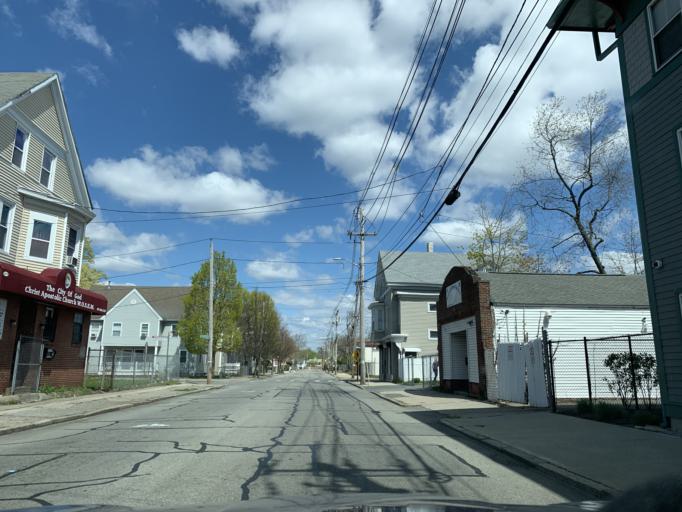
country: US
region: Rhode Island
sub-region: Providence County
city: Providence
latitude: 41.8057
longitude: -71.4148
